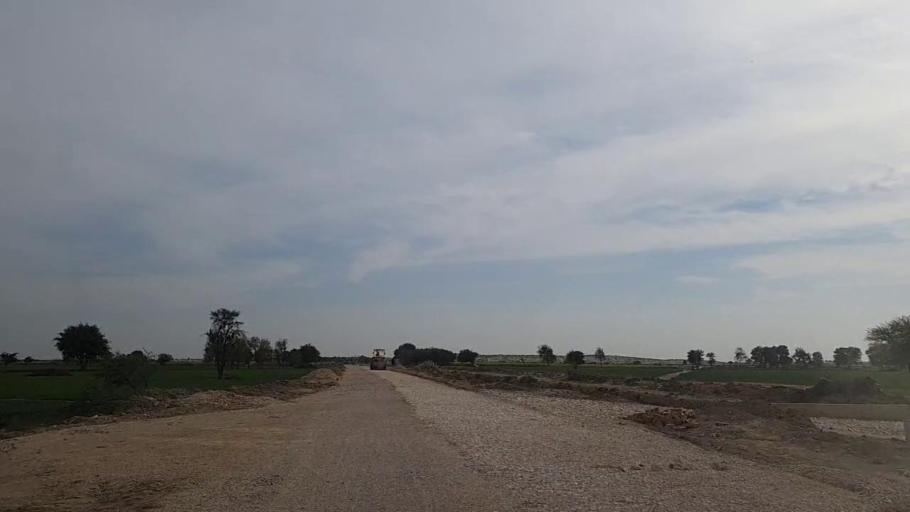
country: PK
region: Sindh
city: Jam Sahib
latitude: 26.4079
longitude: 68.4933
